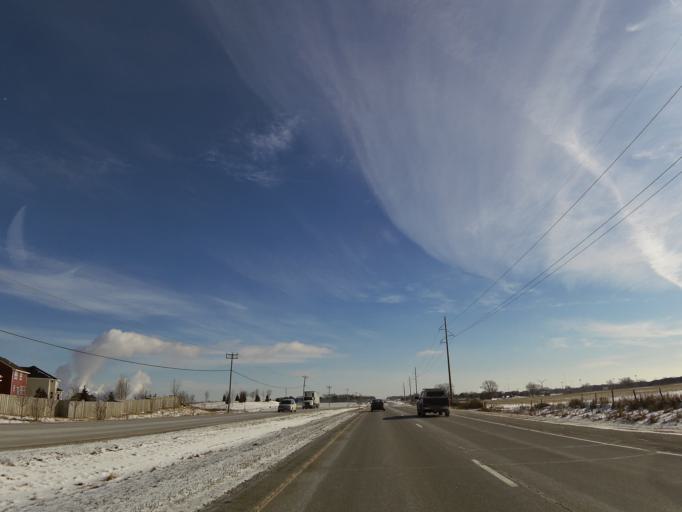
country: US
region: Minnesota
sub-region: Dakota County
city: Rosemount
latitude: 44.7392
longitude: -93.0932
